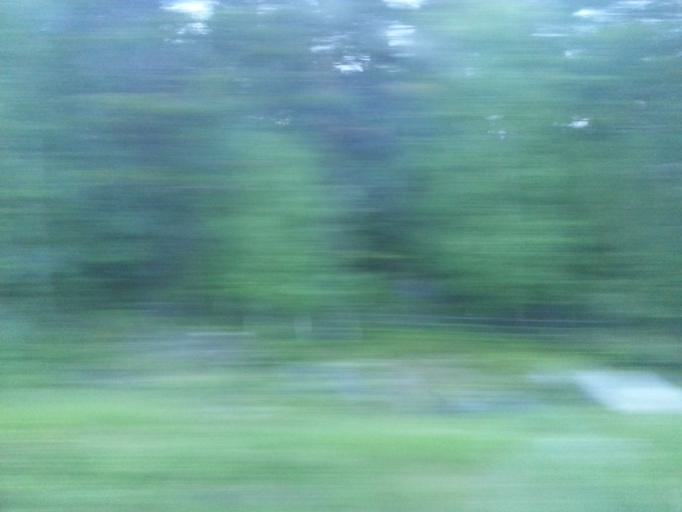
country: NO
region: Oppland
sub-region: Dovre
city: Dombas
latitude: 62.0950
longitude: 9.1353
